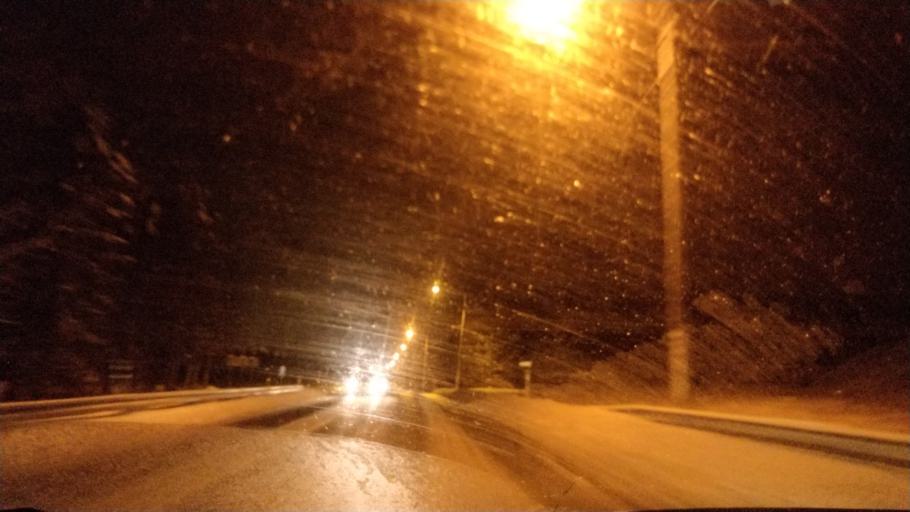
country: FI
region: Lapland
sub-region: Rovaniemi
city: Rovaniemi
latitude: 66.3916
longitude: 25.3793
